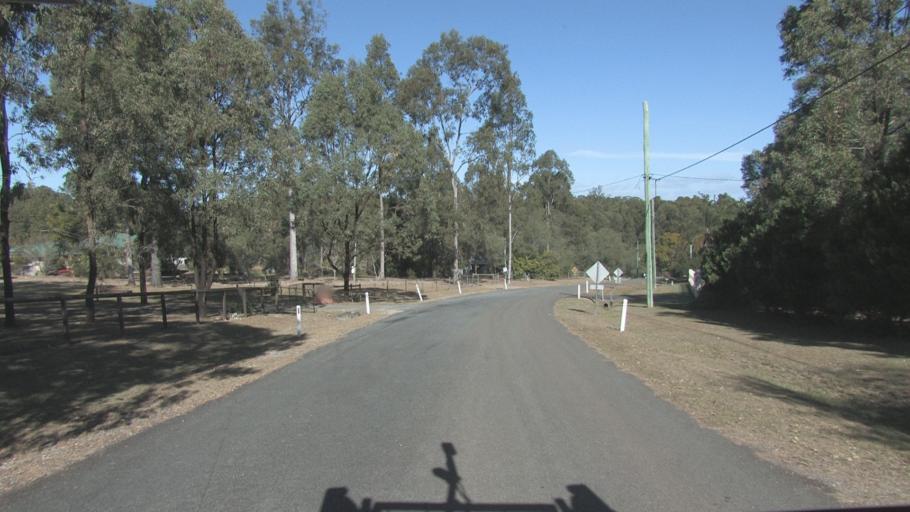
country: AU
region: Queensland
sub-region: Logan
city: Cedar Vale
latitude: -27.8567
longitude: 152.9875
